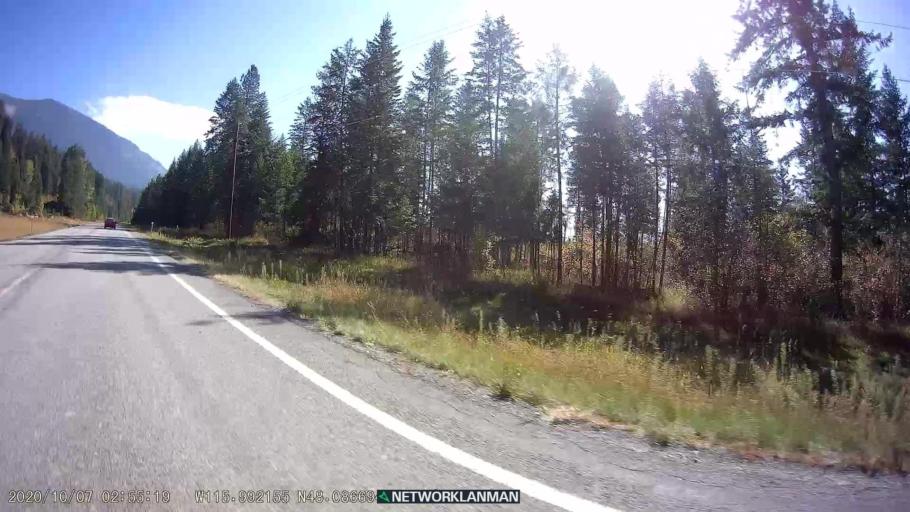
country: US
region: Montana
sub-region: Lincoln County
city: Libby
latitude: 48.0866
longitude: -115.9922
